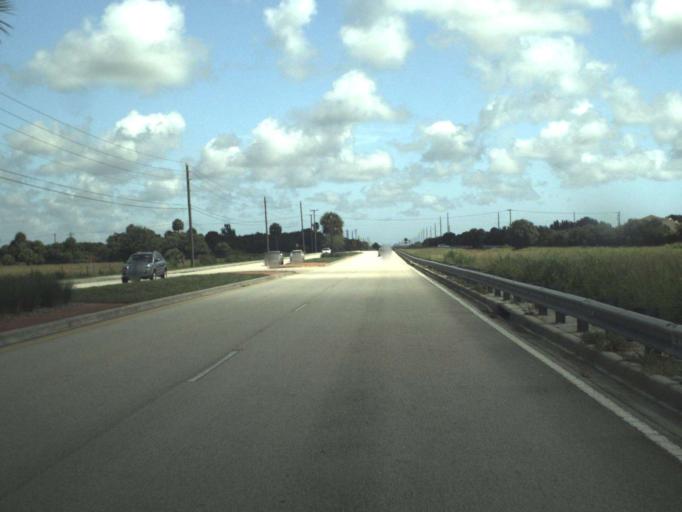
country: US
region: Florida
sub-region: Indian River County
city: Vero Beach South
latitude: 27.5915
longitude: -80.4473
